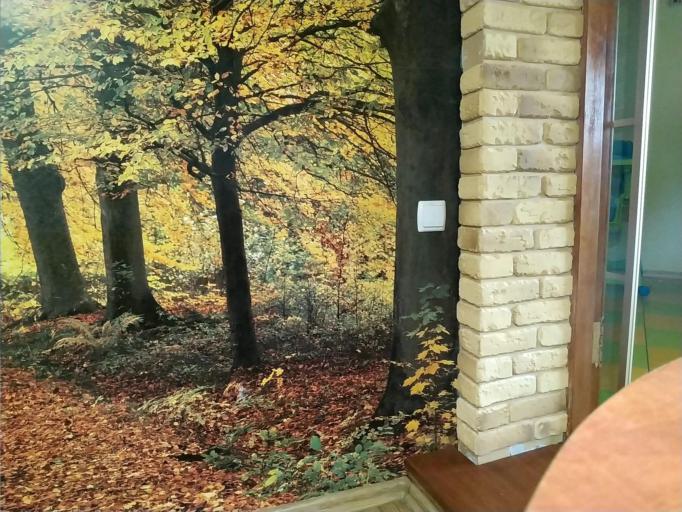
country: RU
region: Smolensk
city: Dorogobuzh
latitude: 54.9419
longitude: 33.3079
